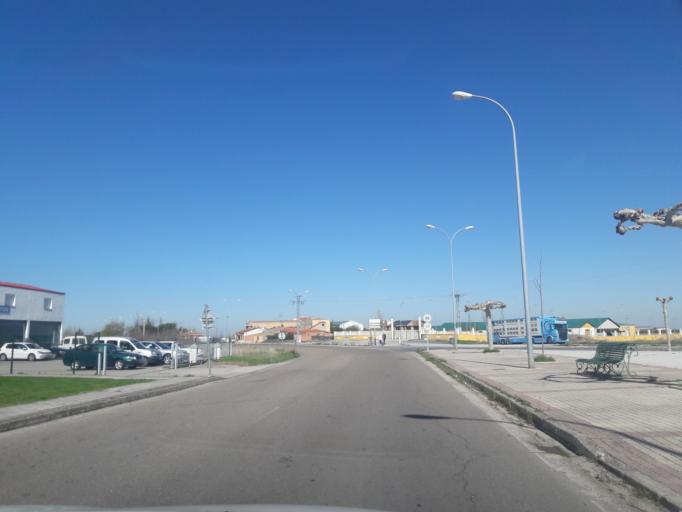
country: ES
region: Castille and Leon
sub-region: Provincia de Salamanca
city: Penaranda de Bracamonte
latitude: 40.9040
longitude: -5.2066
